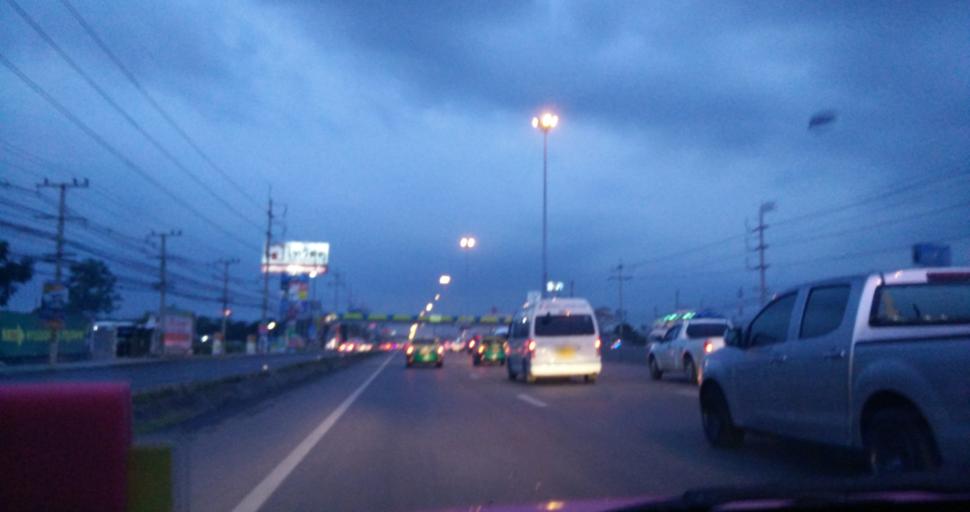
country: TH
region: Pathum Thani
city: Khlong Luang
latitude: 14.0143
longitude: 100.6152
